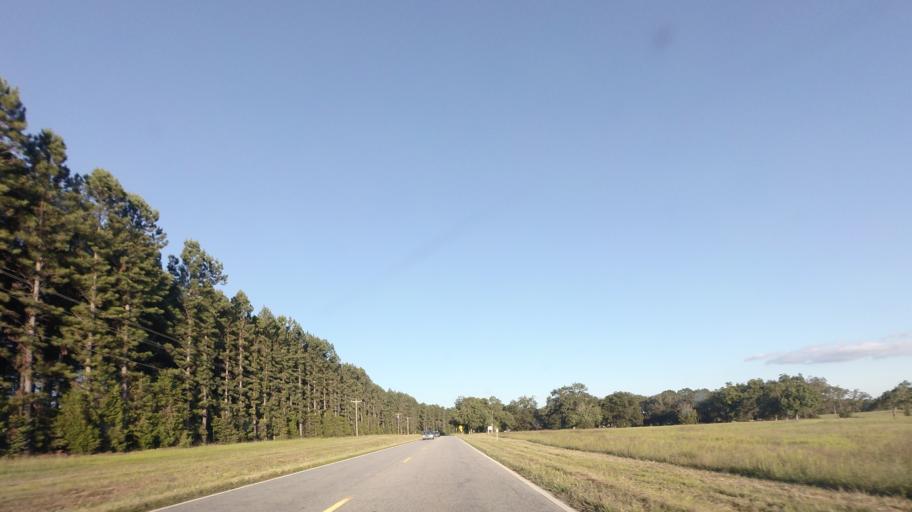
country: US
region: Georgia
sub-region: Spalding County
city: East Griffin
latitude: 33.2892
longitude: -84.1694
